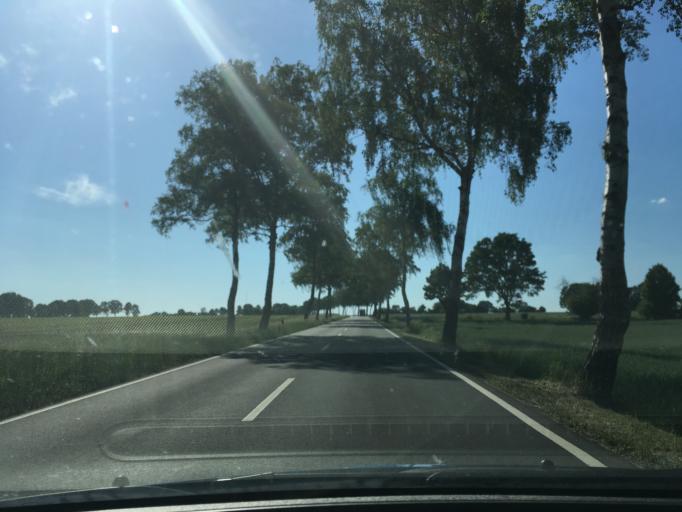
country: DE
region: Lower Saxony
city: Bad Fallingbostel
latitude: 52.9058
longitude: 9.7516
